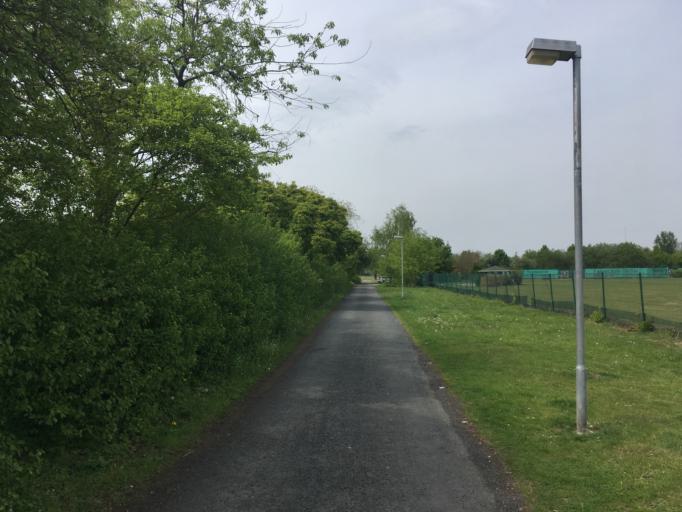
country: DE
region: Lower Saxony
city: Braunschweig
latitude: 52.2959
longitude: 10.5061
